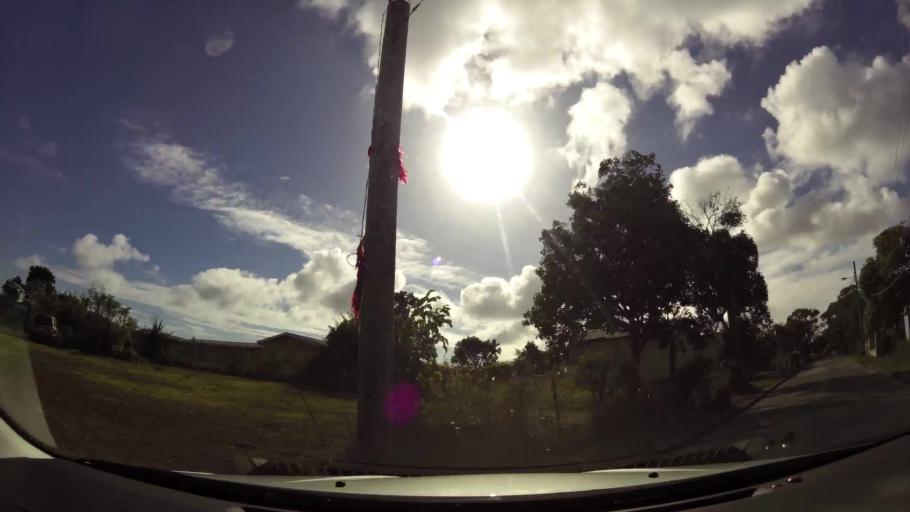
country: AG
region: Saint Peter
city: All Saints
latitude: 17.0640
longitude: -61.7931
